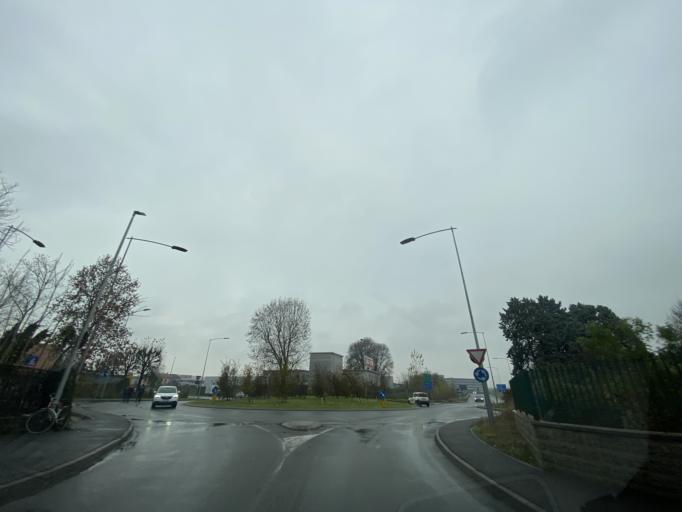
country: IT
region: Lombardy
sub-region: Citta metropolitana di Milano
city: Baranzate
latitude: 45.5270
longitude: 9.1082
